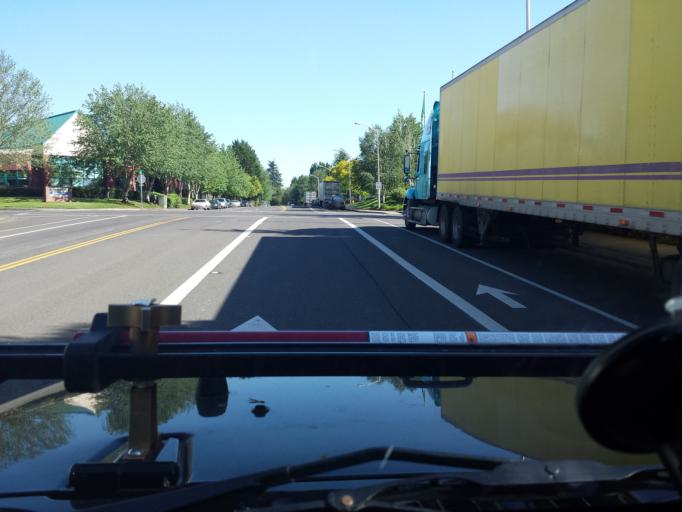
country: US
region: Washington
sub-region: Clark County
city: Walnut Grove
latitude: 45.6542
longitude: -122.5941
